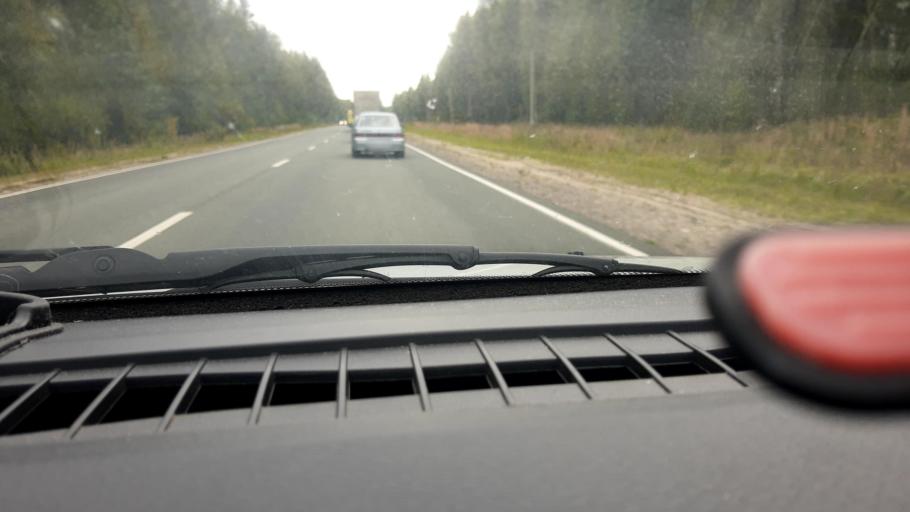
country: RU
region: Nizjnij Novgorod
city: Uren'
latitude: 57.3827
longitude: 45.6882
